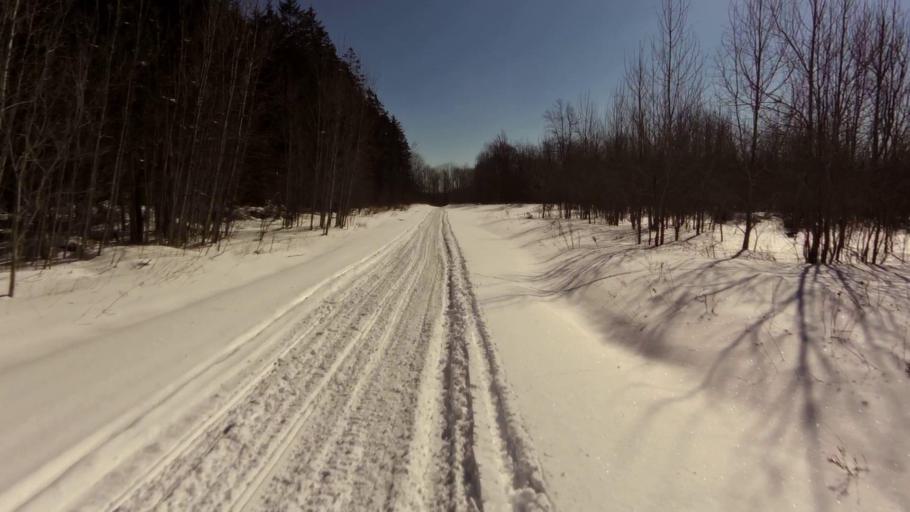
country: US
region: New York
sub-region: Cattaraugus County
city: Franklinville
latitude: 42.3436
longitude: -78.3501
